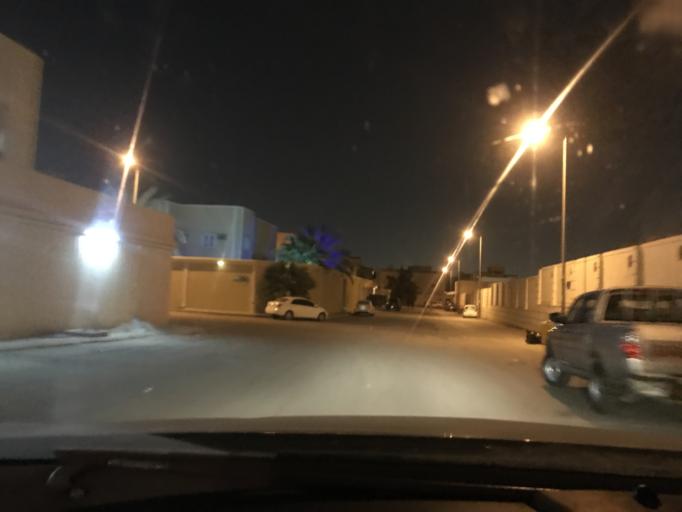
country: SA
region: Ar Riyad
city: Riyadh
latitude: 24.7565
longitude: 46.7526
